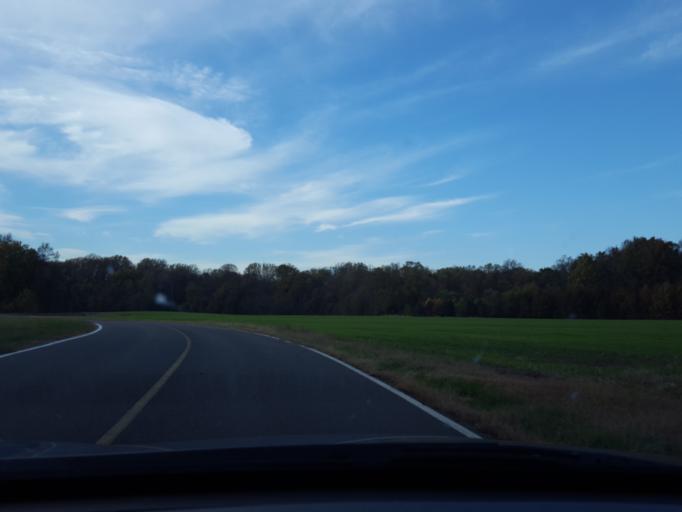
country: US
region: Maryland
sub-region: Prince George's County
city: Kettering
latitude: 38.8813
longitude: -76.7868
